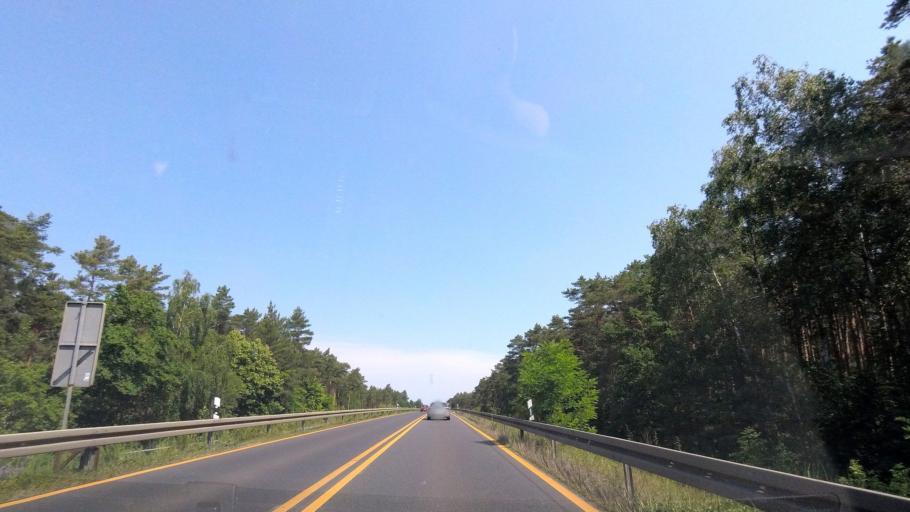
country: DE
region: Berlin
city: Bohnsdorf
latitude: 52.3819
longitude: 13.5631
